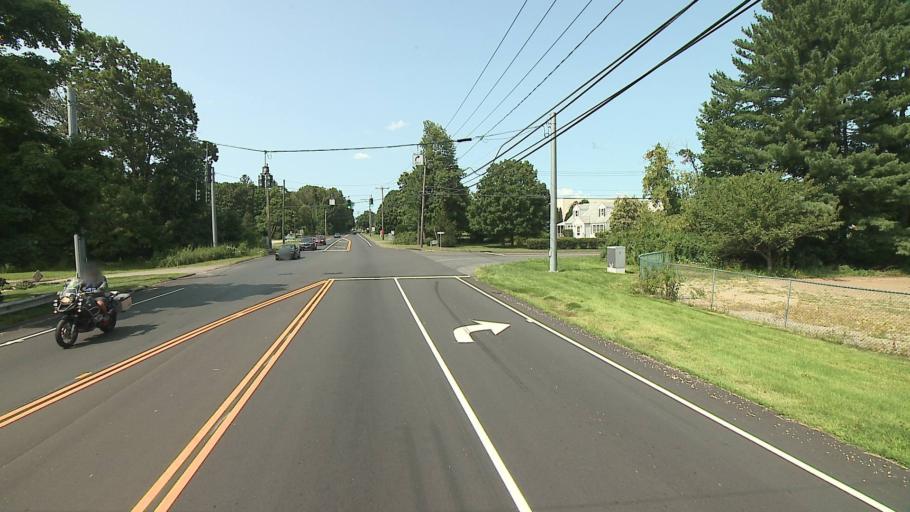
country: US
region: Connecticut
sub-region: Fairfield County
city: Trumbull
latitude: 41.2928
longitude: -73.2437
